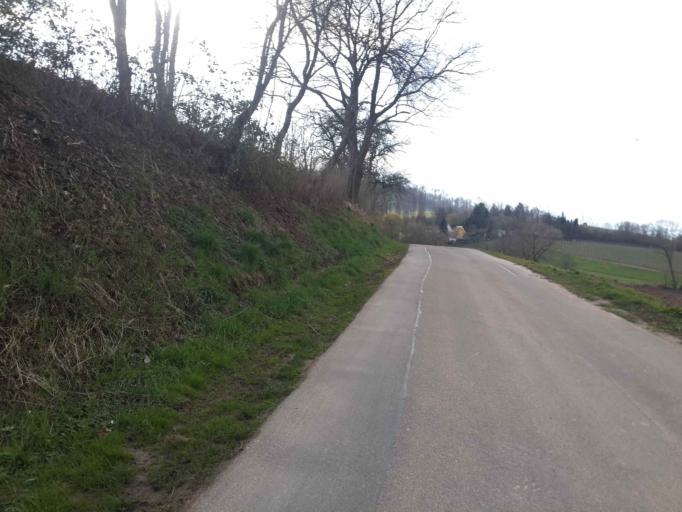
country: DE
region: Baden-Wuerttemberg
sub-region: Regierungsbezirk Stuttgart
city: Erlenbach
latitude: 49.1557
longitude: 9.2672
